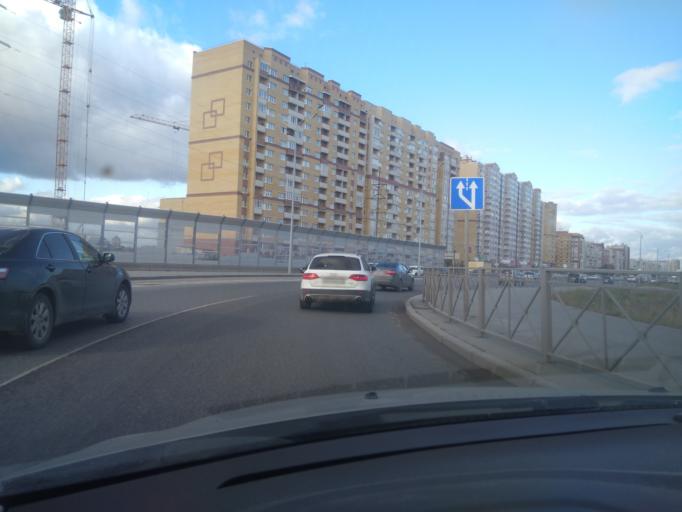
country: RU
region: Tjumen
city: Tyumen
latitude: 57.1143
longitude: 65.5392
